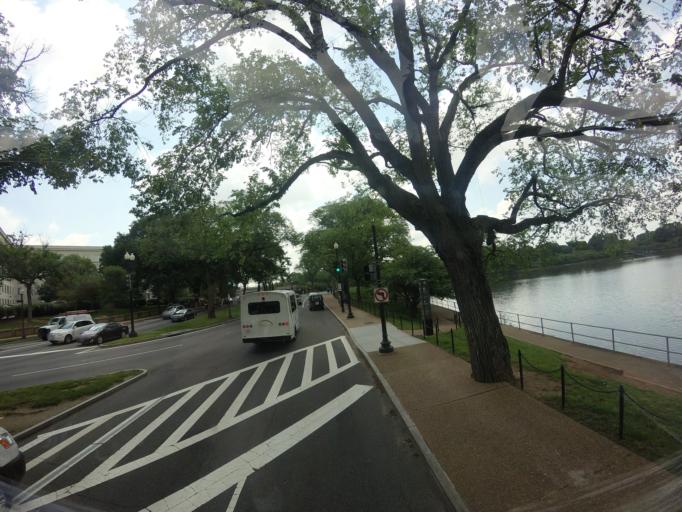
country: US
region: Washington, D.C.
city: Washington, D.C.
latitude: 38.8845
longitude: -77.0339
